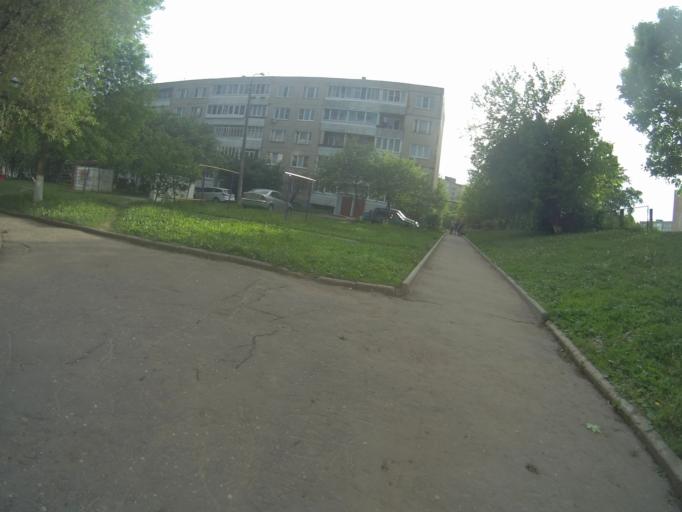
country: RU
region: Vladimir
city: Kommunar
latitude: 56.1613
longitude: 40.4540
